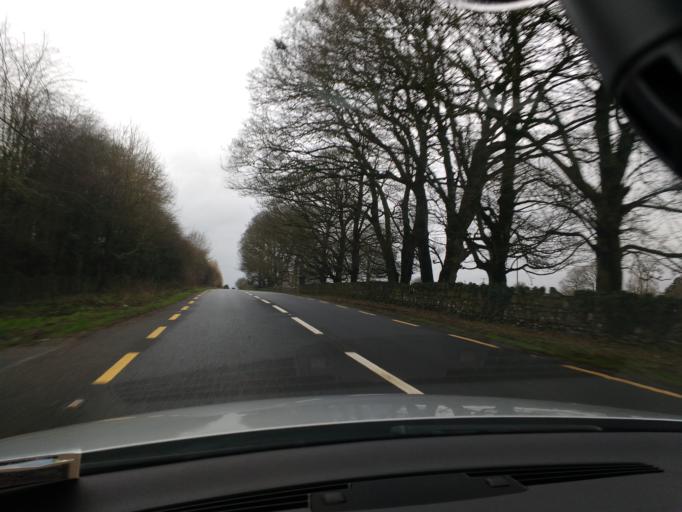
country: IE
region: Munster
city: Thurles
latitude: 52.6730
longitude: -7.7562
